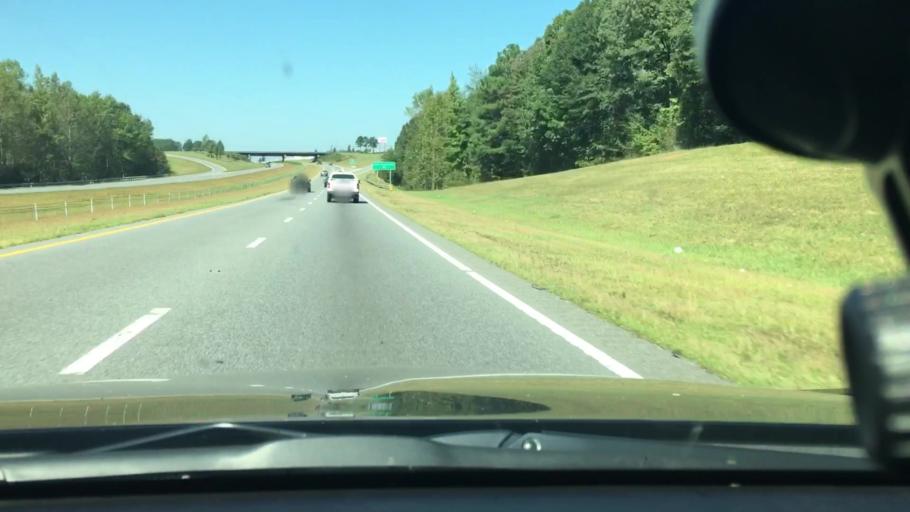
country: US
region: North Carolina
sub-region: Cleveland County
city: Kings Mountain
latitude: 35.2549
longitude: -81.3531
